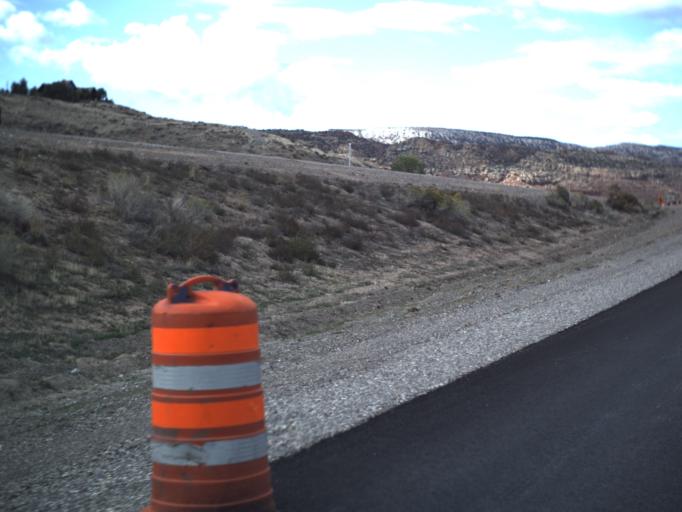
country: US
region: Utah
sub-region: Sevier County
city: Richfield
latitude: 38.7515
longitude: -112.1047
